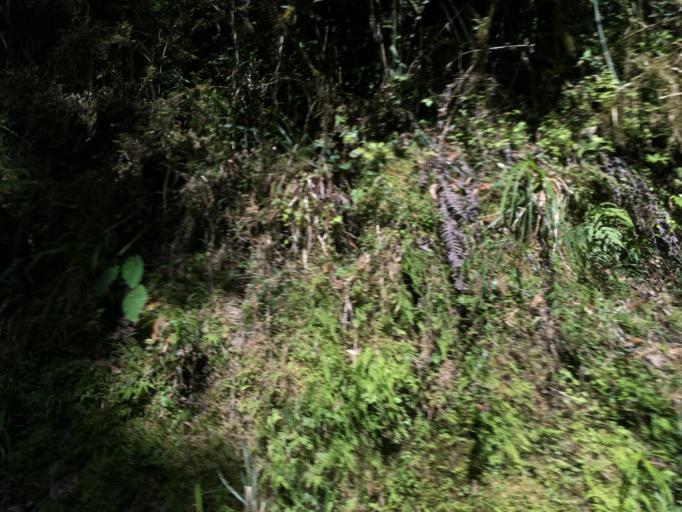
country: TW
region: Taiwan
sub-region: Yilan
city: Yilan
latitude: 24.6199
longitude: 121.4756
